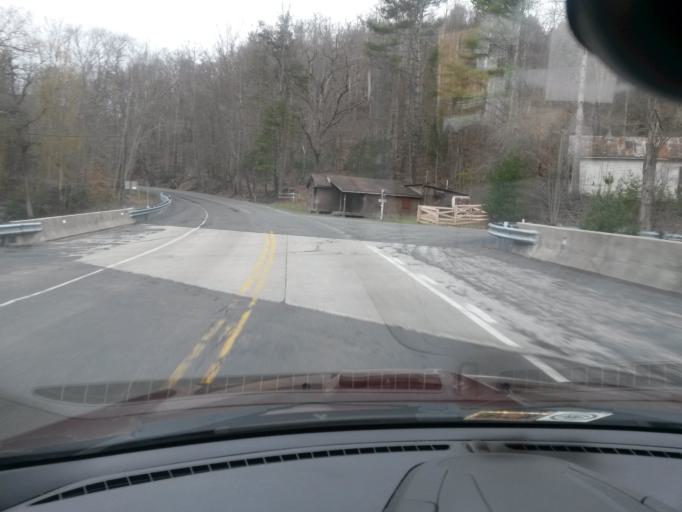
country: US
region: Virginia
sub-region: Bath County
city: Warm Springs
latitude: 38.1719
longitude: -79.7390
